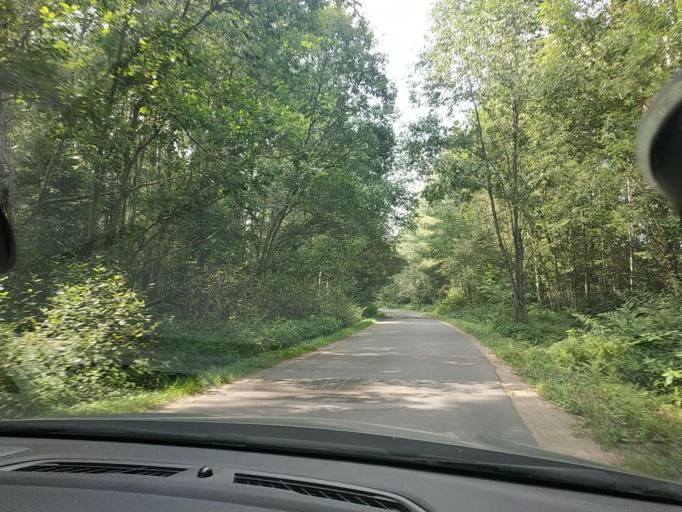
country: LT
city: Nemencine
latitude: 54.8520
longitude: 25.4496
